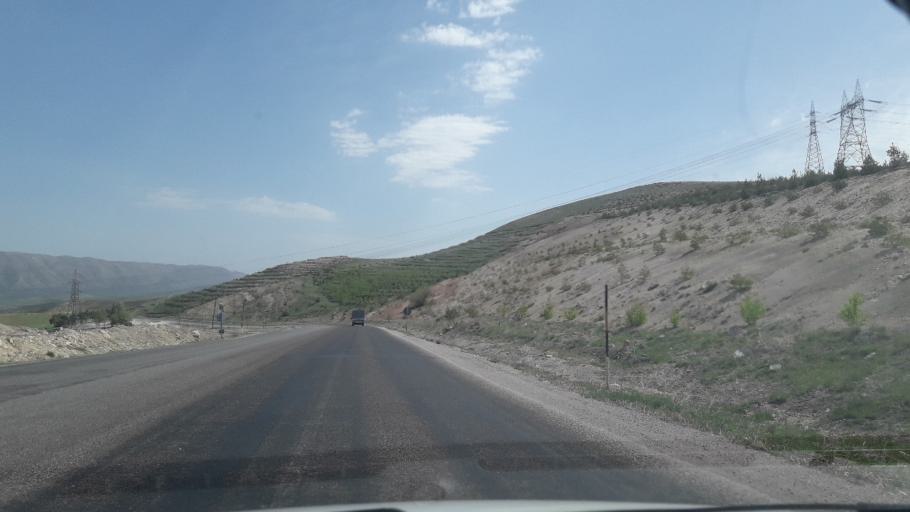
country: TR
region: Sivas
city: Deliktas
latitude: 39.3241
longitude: 37.1442
